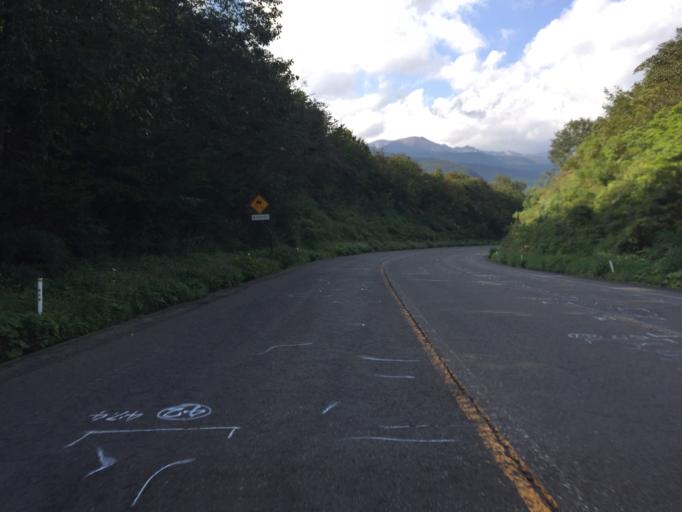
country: JP
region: Fukushima
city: Nihommatsu
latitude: 37.6670
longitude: 140.3262
